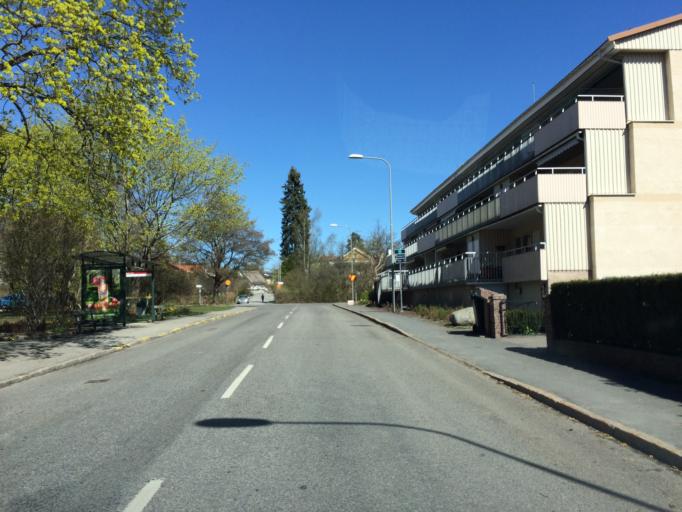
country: SE
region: Stockholm
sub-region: Huddinge Kommun
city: Huddinge
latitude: 59.2689
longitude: 17.9701
